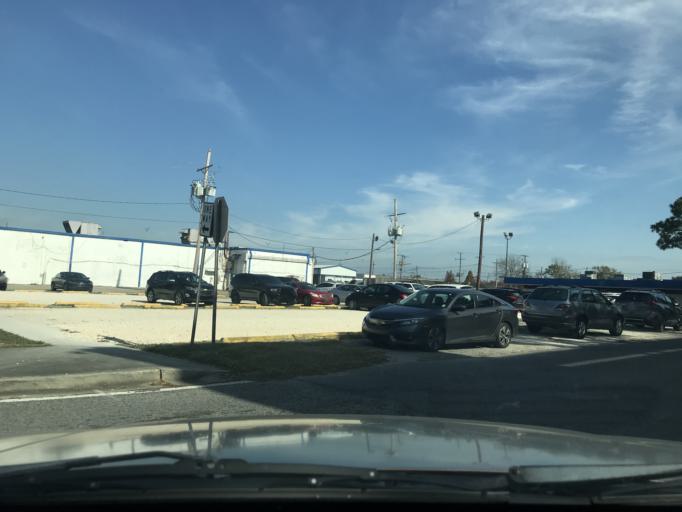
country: US
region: Louisiana
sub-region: Jefferson Parish
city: Marrero
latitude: 29.8929
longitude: -90.0961
